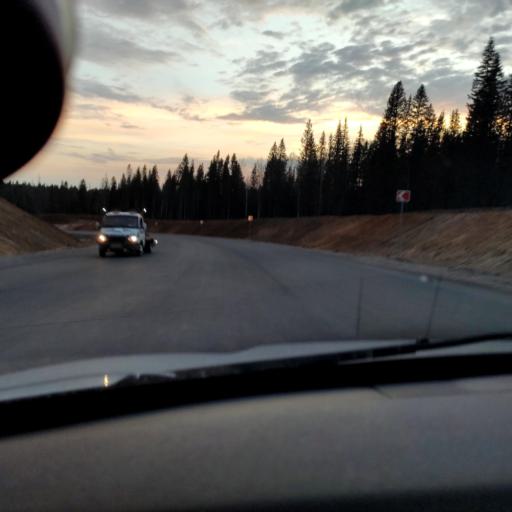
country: RU
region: Perm
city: Chusovoy
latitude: 58.3394
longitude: 57.8008
